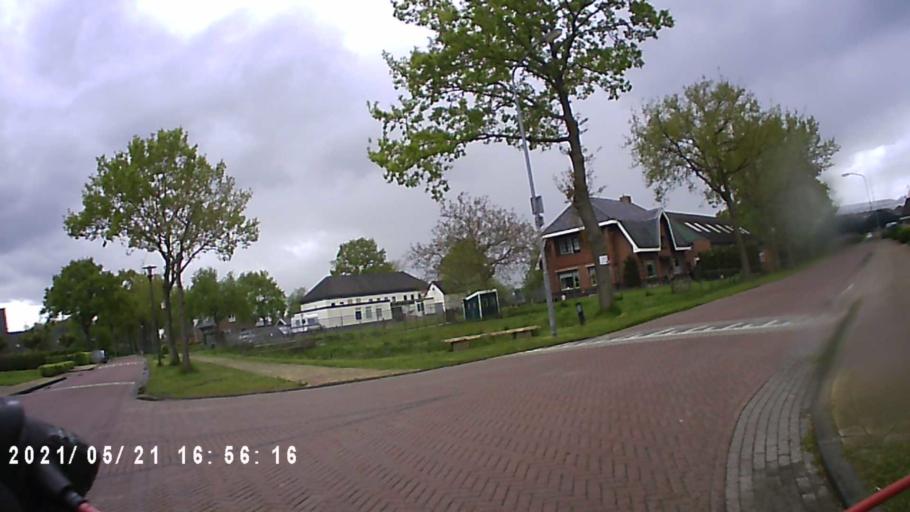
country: NL
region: Groningen
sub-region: Gemeente Zuidhorn
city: Aduard
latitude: 53.1677
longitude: 6.4686
